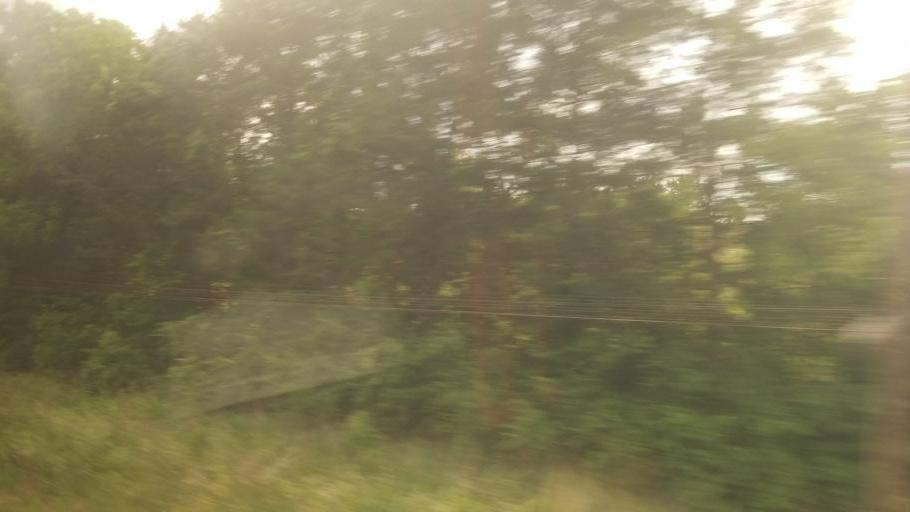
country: US
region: Kansas
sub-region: Osage County
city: Carbondale
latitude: 38.8788
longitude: -95.6904
